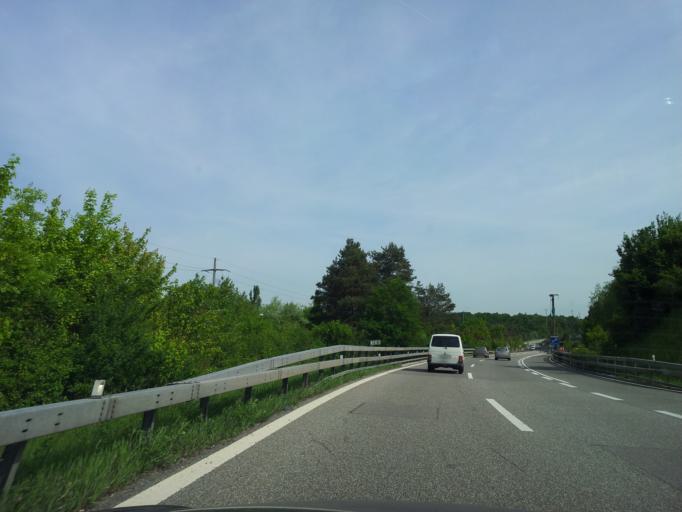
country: CH
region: Zurich
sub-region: Bezirk Buelach
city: Buelach / Niederflachs
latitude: 47.5149
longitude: 8.5255
